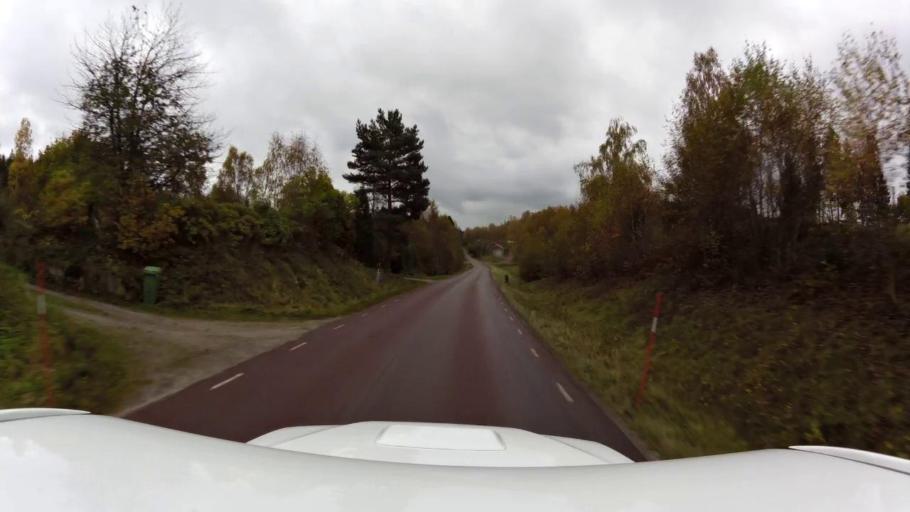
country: SE
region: OEstergoetland
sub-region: Linkopings Kommun
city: Ljungsbro
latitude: 58.5659
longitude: 15.5157
